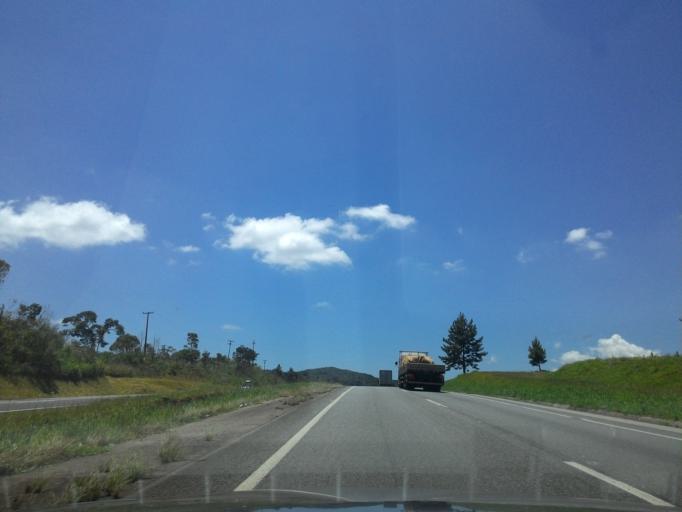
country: BR
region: Parana
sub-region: Antonina
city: Antonina
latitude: -25.0822
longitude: -48.5991
